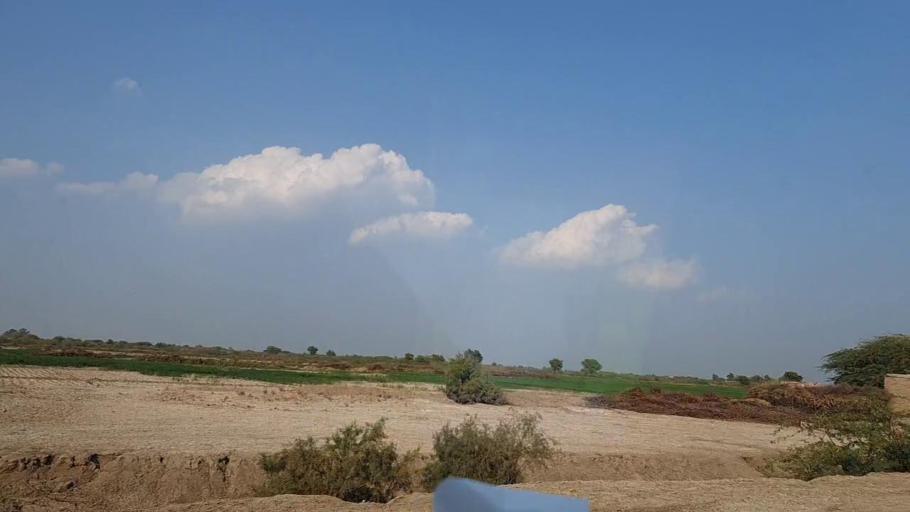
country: PK
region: Sindh
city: Nawabshah
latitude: 26.1632
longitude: 68.4133
